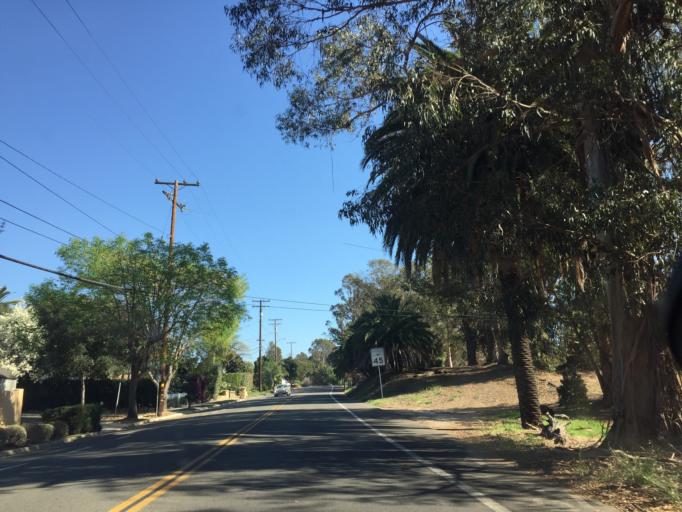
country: US
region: California
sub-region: Santa Barbara County
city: Mission Canyon
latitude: 34.4375
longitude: -119.7637
